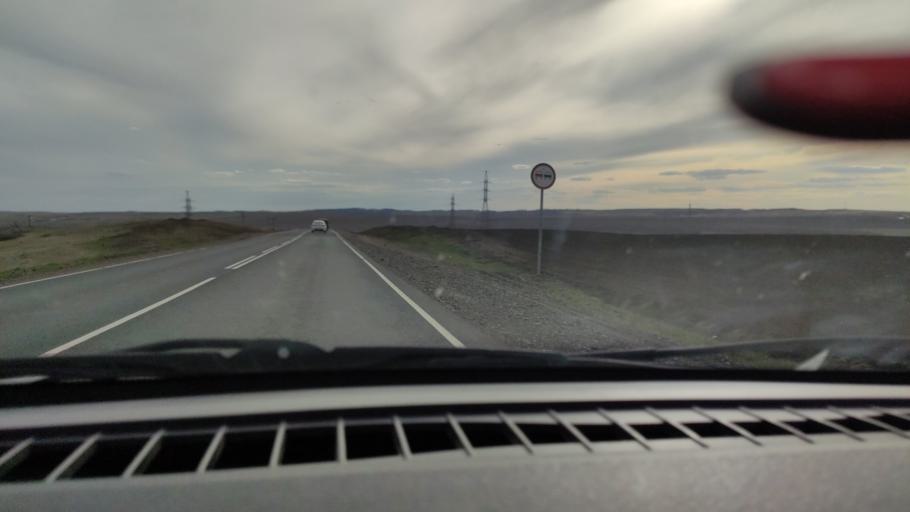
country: RU
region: Bashkortostan
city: Yermolayevo
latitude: 52.6729
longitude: 55.8449
